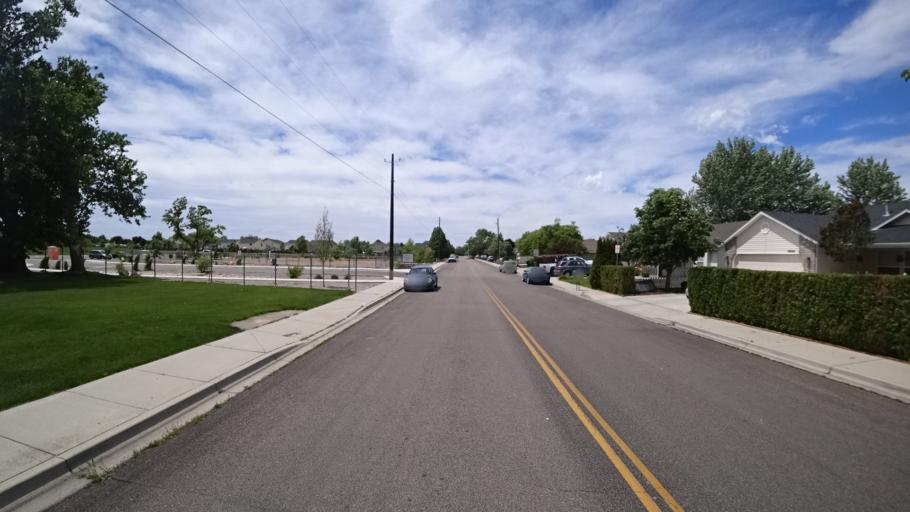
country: US
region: Idaho
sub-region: Ada County
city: Garden City
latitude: 43.6157
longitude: -116.3044
